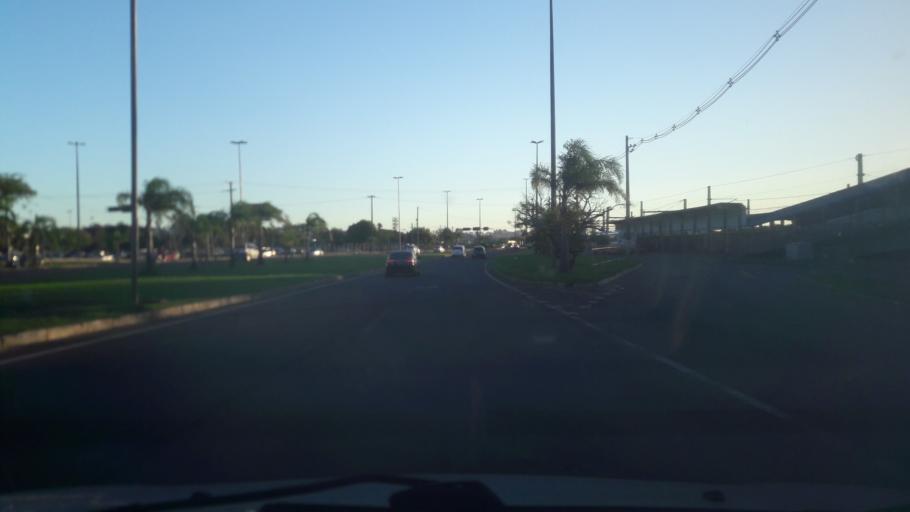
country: BR
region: Rio Grande do Sul
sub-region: Porto Alegre
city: Porto Alegre
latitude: -29.9881
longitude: -51.1826
